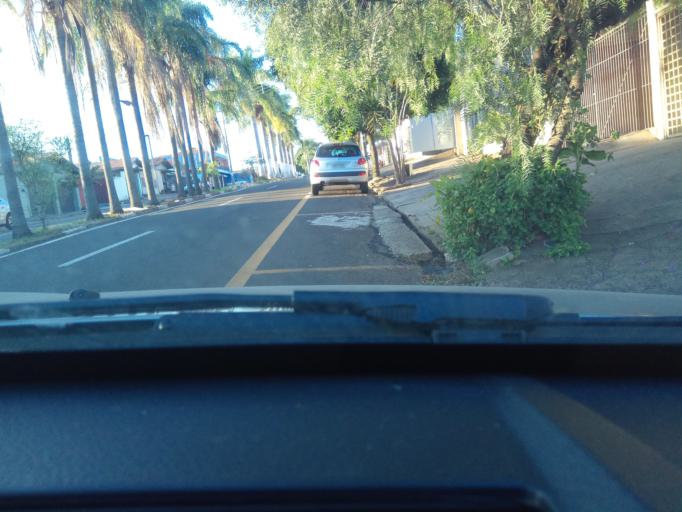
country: BR
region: Sao Paulo
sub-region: Piracicaba
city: Piracicaba
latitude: -22.7378
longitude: -47.6648
